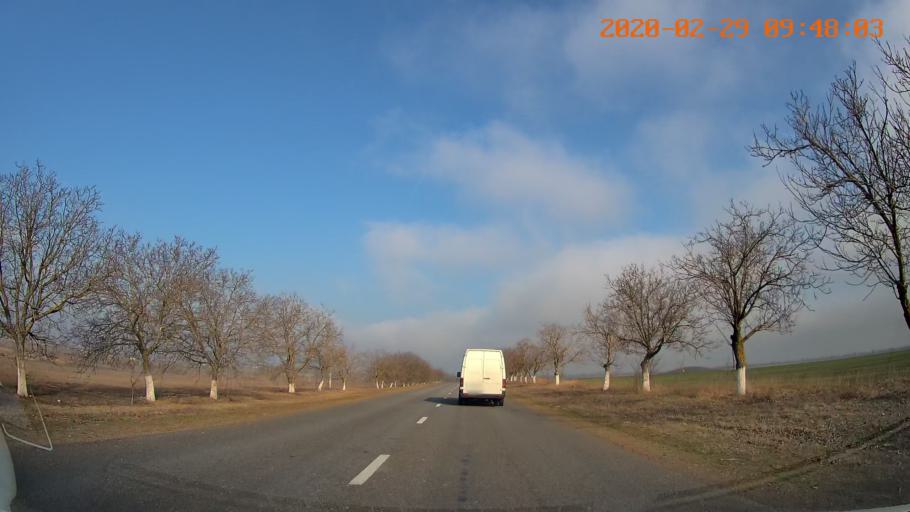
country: MD
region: Telenesti
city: Crasnoe
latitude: 46.6832
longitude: 29.7869
